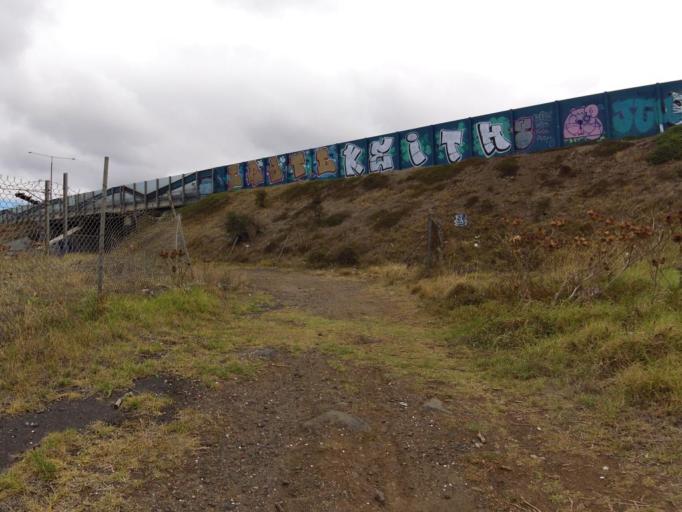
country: AU
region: Victoria
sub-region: Hobsons Bay
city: Laverton
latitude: -37.8621
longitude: 144.7776
